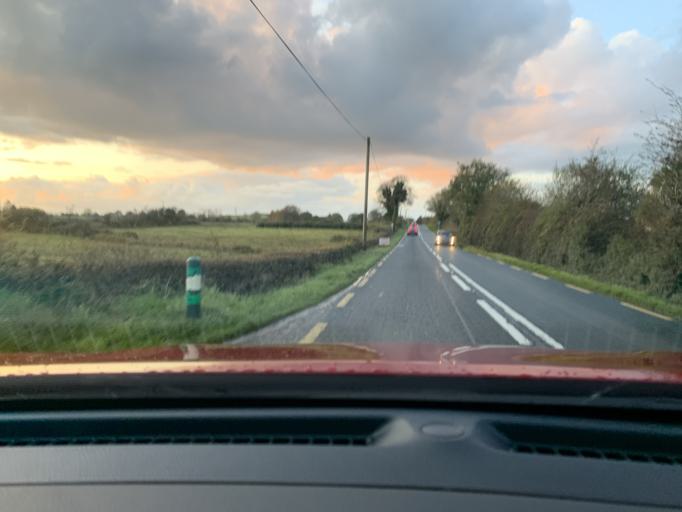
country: IE
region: Connaught
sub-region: Sligo
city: Ballymote
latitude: 54.1081
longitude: -8.4150
